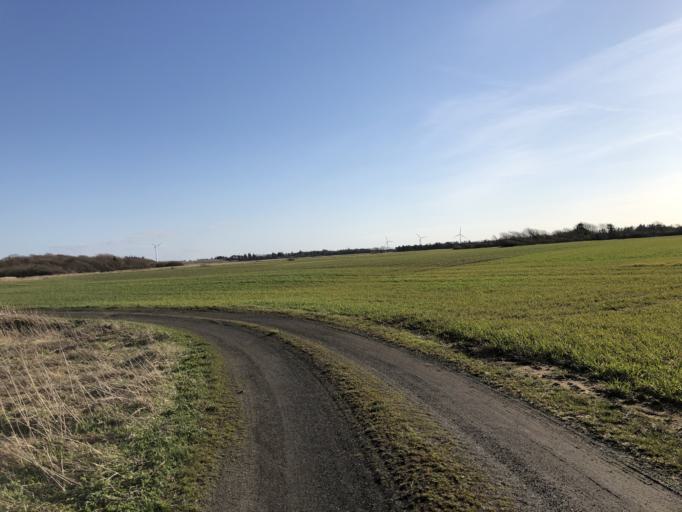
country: DK
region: Central Jutland
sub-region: Holstebro Kommune
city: Ulfborg
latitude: 56.3322
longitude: 8.3257
